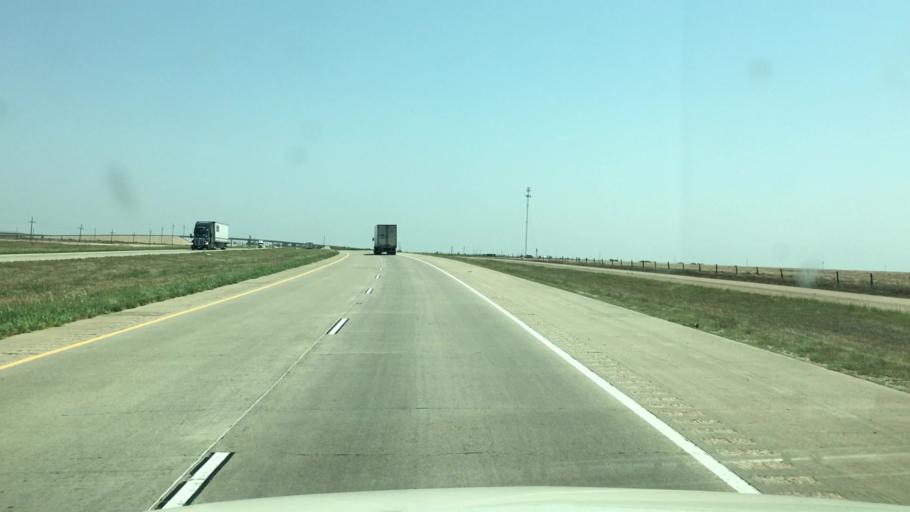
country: US
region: Texas
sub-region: Oldham County
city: Vega
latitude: 35.2106
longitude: -102.2491
